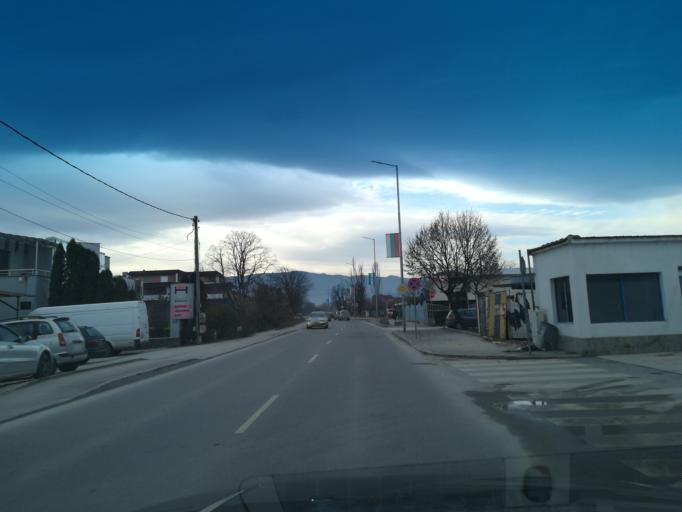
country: BG
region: Plovdiv
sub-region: Obshtina Plovdiv
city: Plovdiv
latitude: 42.1168
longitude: 24.7133
